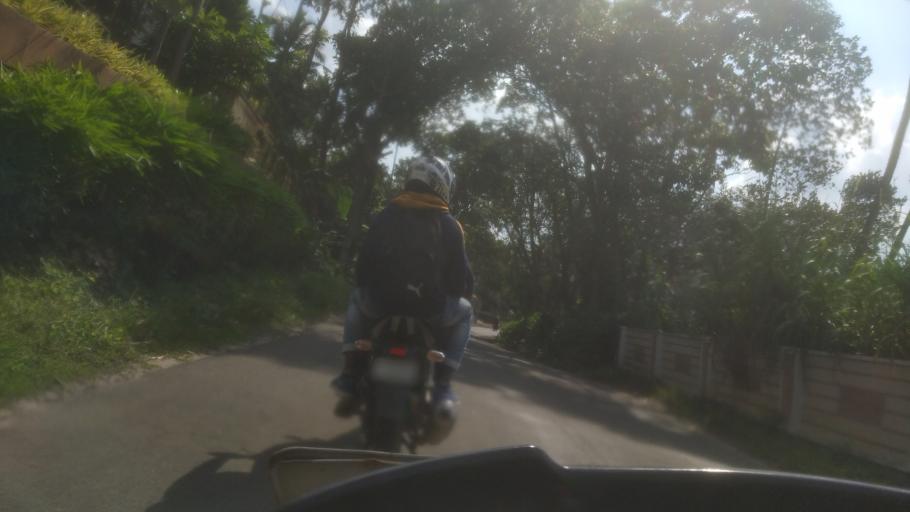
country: IN
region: Kerala
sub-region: Ernakulam
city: Kotamangalam
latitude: 10.0022
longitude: 76.7289
